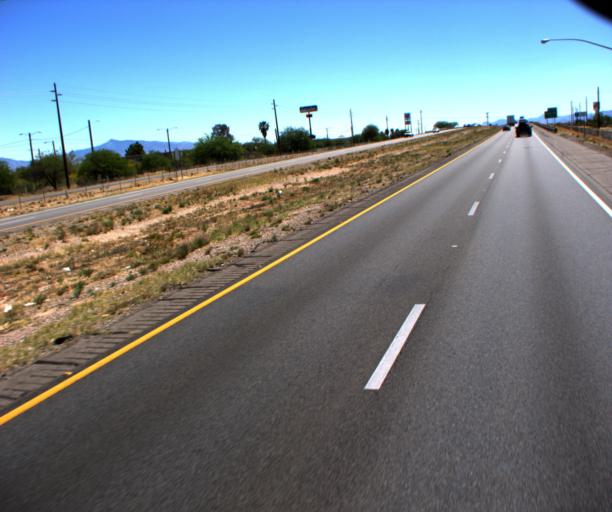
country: US
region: Arizona
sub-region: Pima County
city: Summit
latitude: 32.1174
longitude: -110.8628
